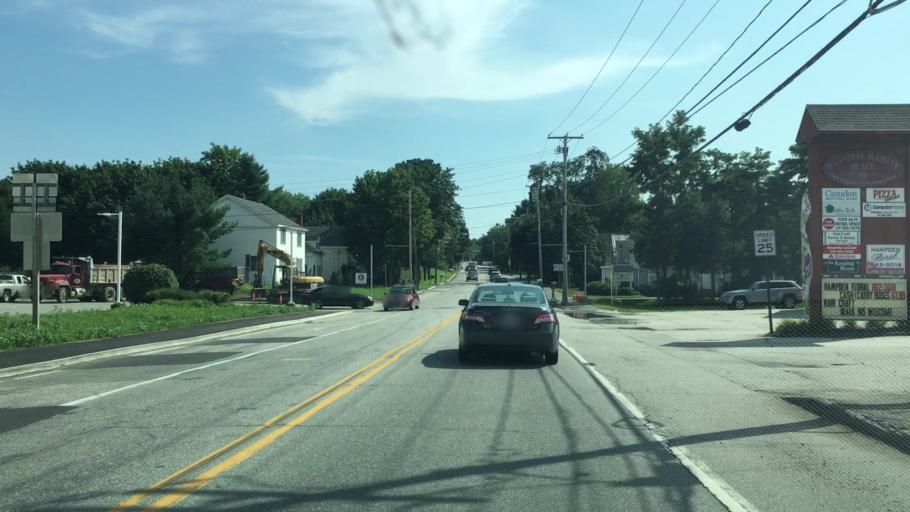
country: US
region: Maine
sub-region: Penobscot County
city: Hampden
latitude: 44.7444
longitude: -68.8378
